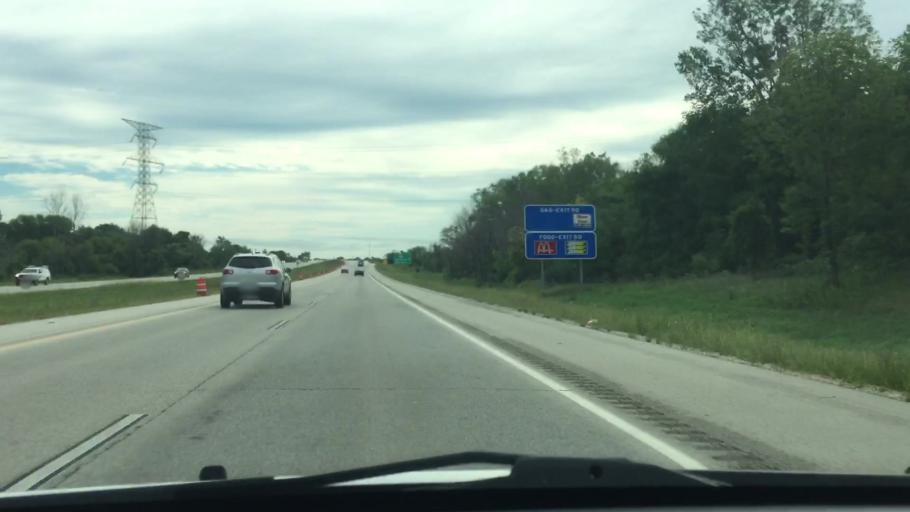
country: US
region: Wisconsin
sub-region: Waukesha County
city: Big Bend
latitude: 42.9084
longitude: -88.2260
